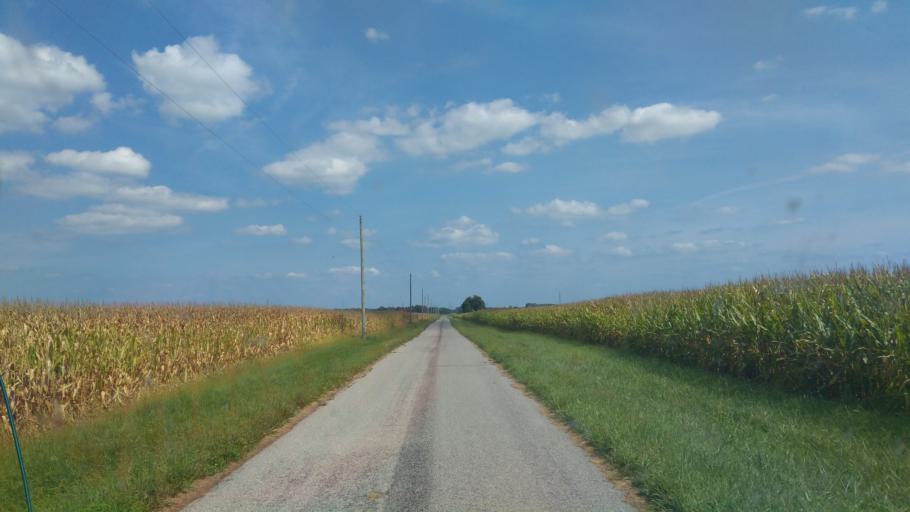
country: US
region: Ohio
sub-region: Union County
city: Richwood
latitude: 40.3970
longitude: -83.4387
